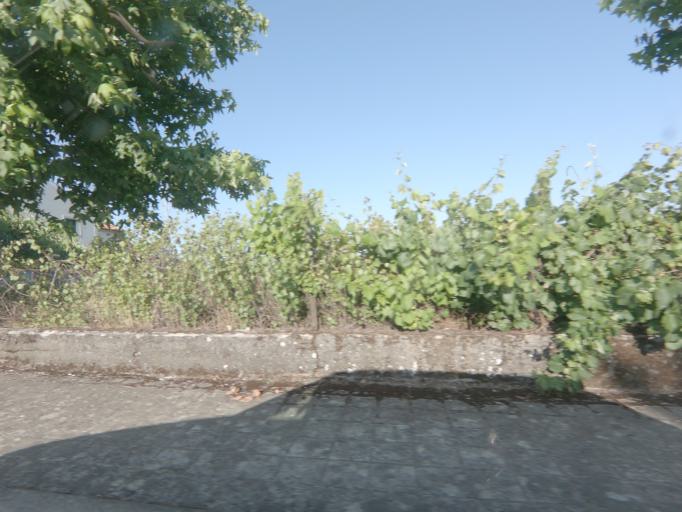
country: PT
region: Vila Real
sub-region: Sabrosa
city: Vilela
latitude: 41.2639
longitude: -7.6204
